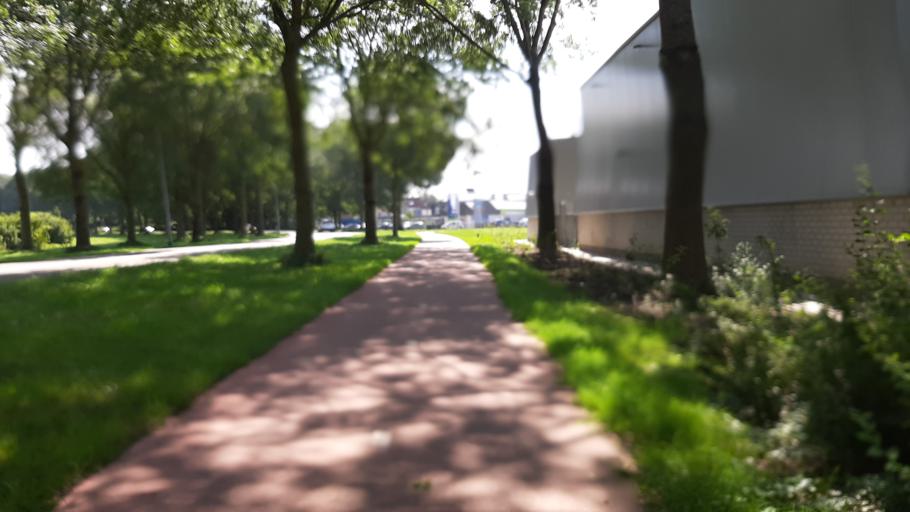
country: NL
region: Flevoland
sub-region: Gemeente Zeewolde
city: Zeewolde
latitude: 52.3375
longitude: 5.5291
